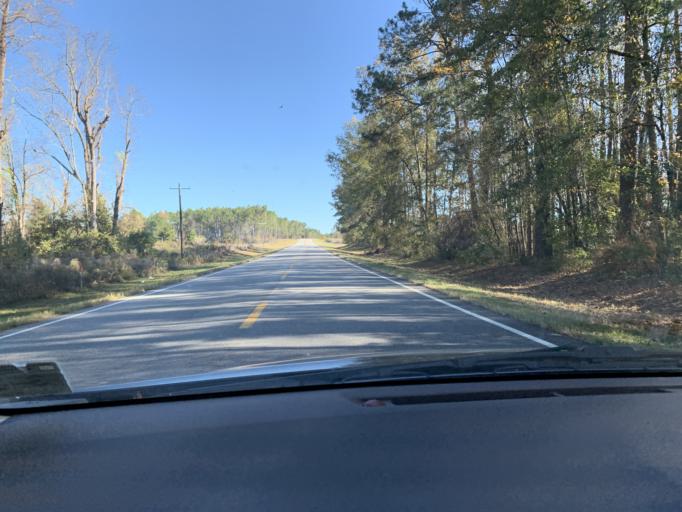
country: US
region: Georgia
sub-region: Ben Hill County
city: Fitzgerald
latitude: 31.7753
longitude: -83.0908
